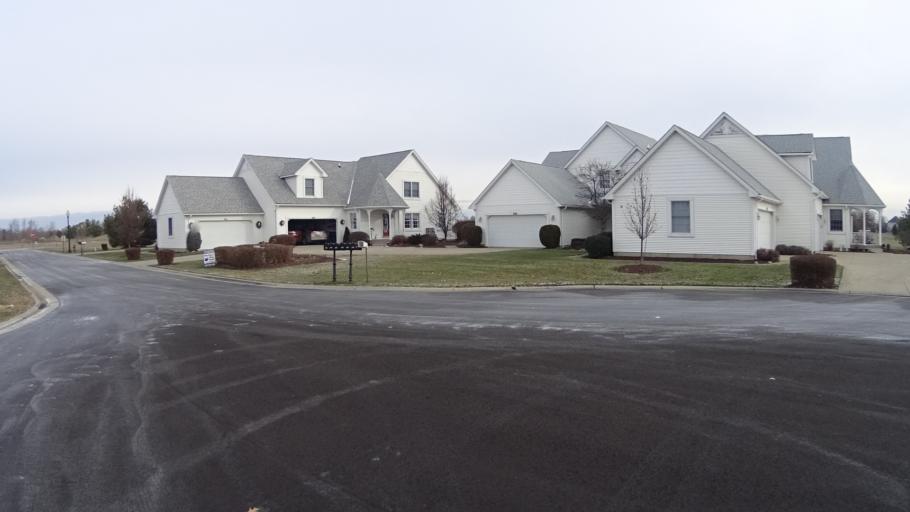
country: US
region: Ohio
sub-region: Lorain County
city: Lagrange
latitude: 41.2469
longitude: -82.1179
